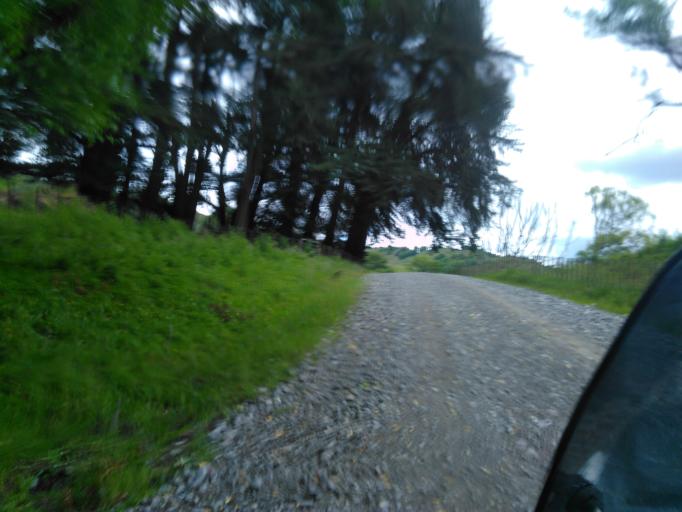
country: NZ
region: Gisborne
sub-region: Gisborne District
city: Gisborne
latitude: -38.0774
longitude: 178.0527
